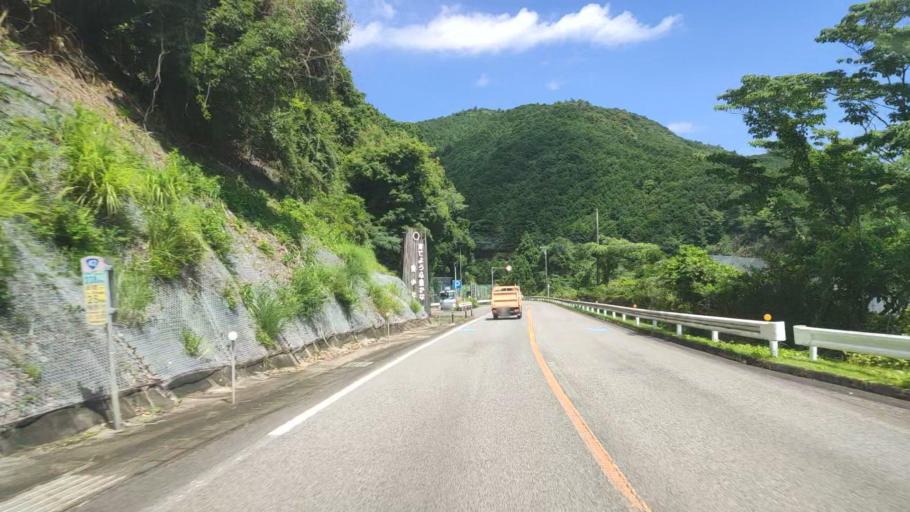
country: JP
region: Mie
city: Owase
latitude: 33.9179
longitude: 136.1112
